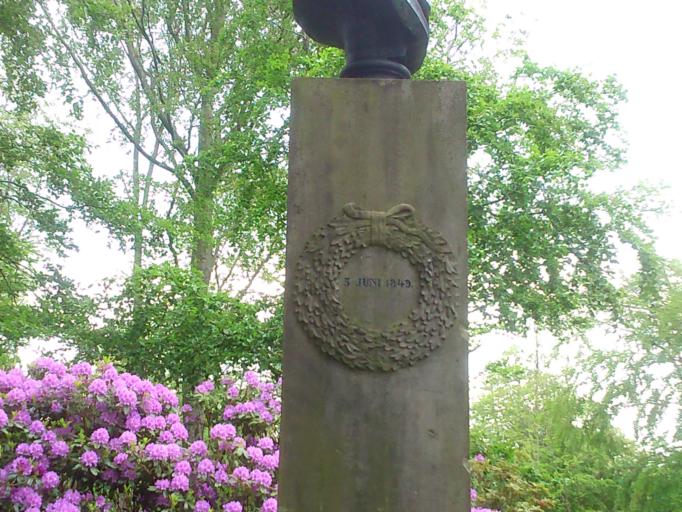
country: DK
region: Central Jutland
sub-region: Ringkobing-Skjern Kommune
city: Skjern
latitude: 55.9450
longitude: 8.4993
